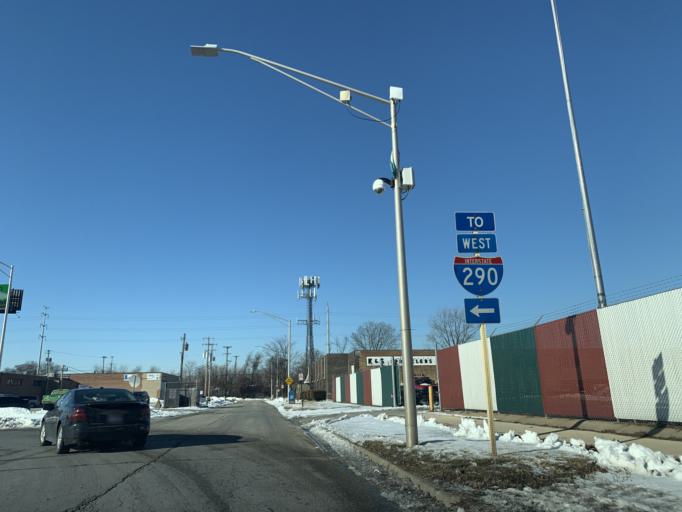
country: US
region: Illinois
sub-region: Cook County
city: Broadview
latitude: 41.8723
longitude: -87.8642
